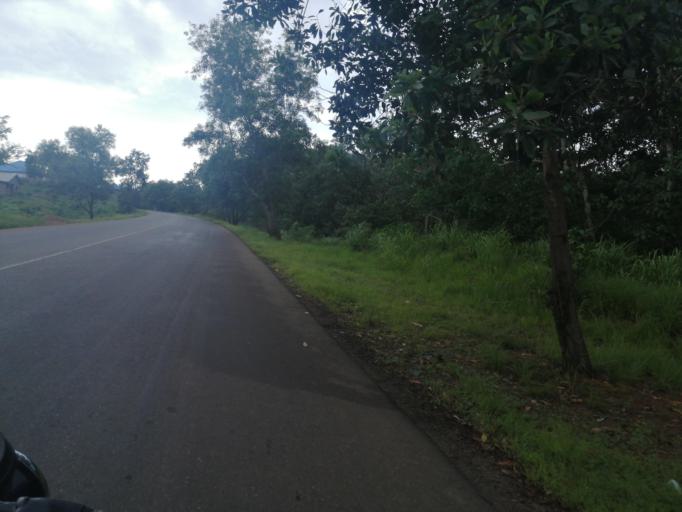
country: SL
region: Northern Province
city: Port Loko
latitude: 8.7663
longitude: -12.7724
